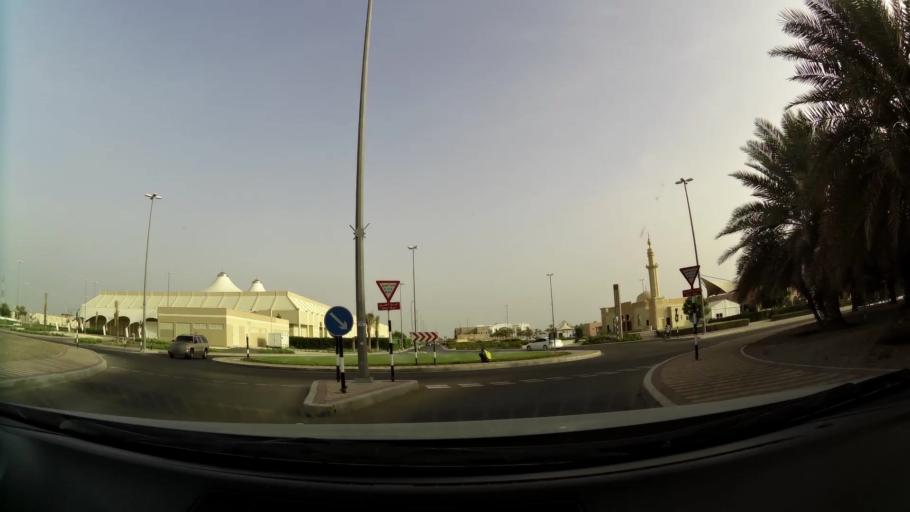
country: AE
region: Abu Dhabi
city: Al Ain
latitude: 24.2383
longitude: 55.7234
